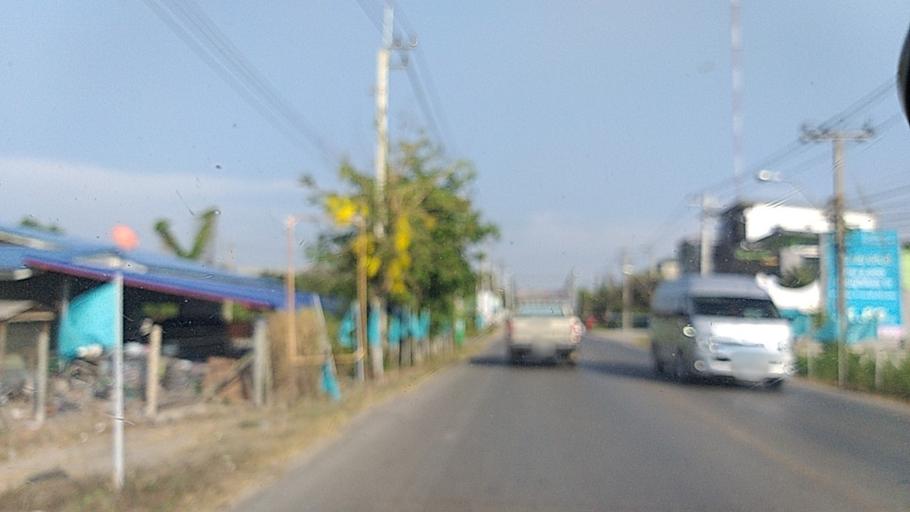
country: TH
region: Nonthaburi
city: Bang Bua Thong
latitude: 13.9372
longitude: 100.3670
